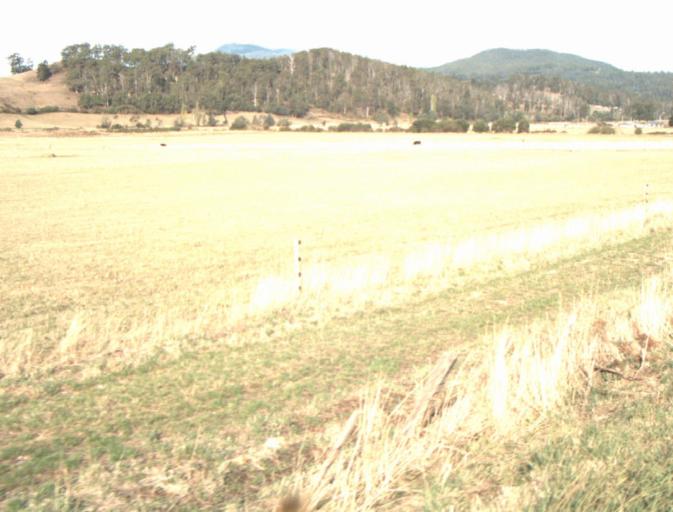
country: AU
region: Tasmania
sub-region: Launceston
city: Mayfield
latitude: -41.2424
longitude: 147.1387
